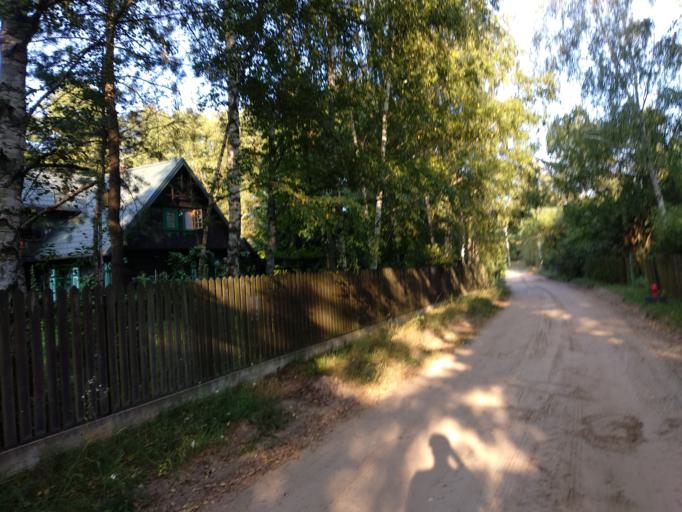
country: PL
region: Masovian Voivodeship
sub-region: Powiat pultuski
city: Obryte
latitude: 52.7558
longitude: 21.1903
